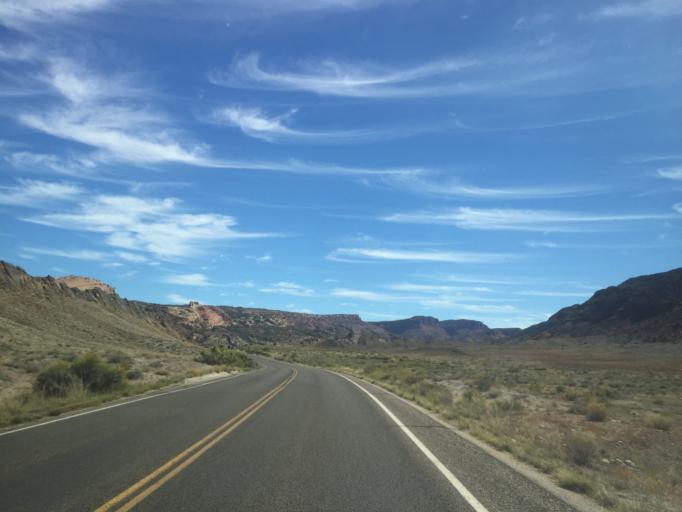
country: US
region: Utah
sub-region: Grand County
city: Moab
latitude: 38.7332
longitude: -109.5080
